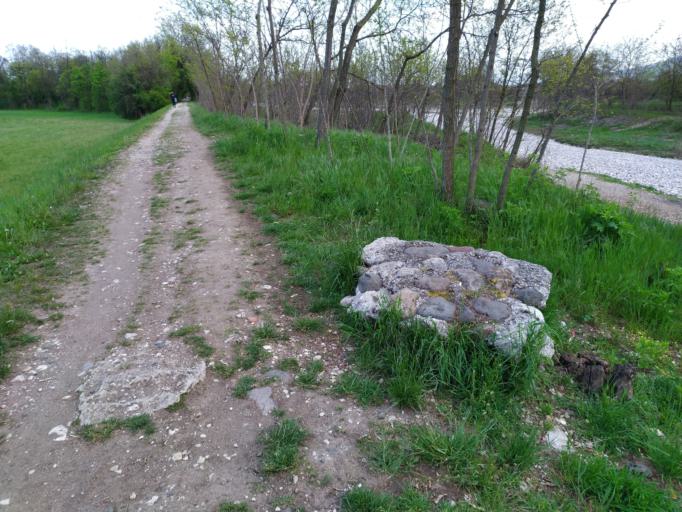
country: IT
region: Veneto
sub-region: Provincia di Vicenza
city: Marano Vicentino
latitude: 45.6816
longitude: 11.4262
